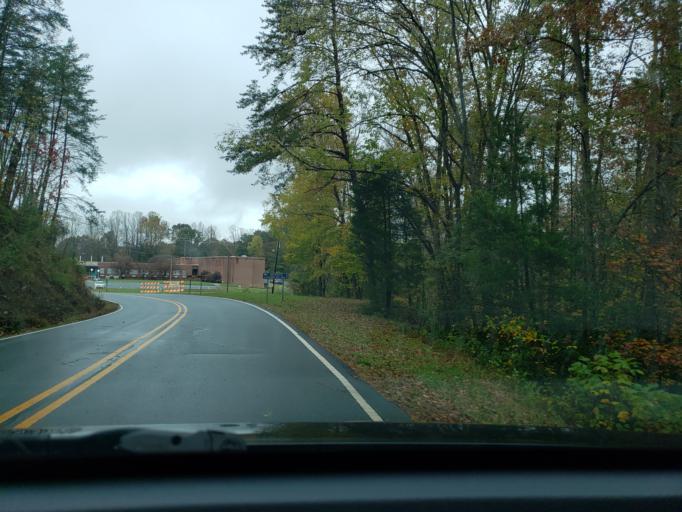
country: US
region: North Carolina
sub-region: Stokes County
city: Danbury
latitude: 36.4163
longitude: -80.2313
